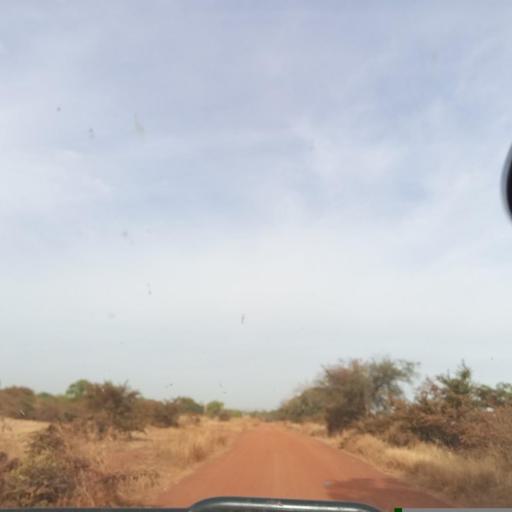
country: ML
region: Koulikoro
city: Koulikoro
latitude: 13.1061
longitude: -7.6457
